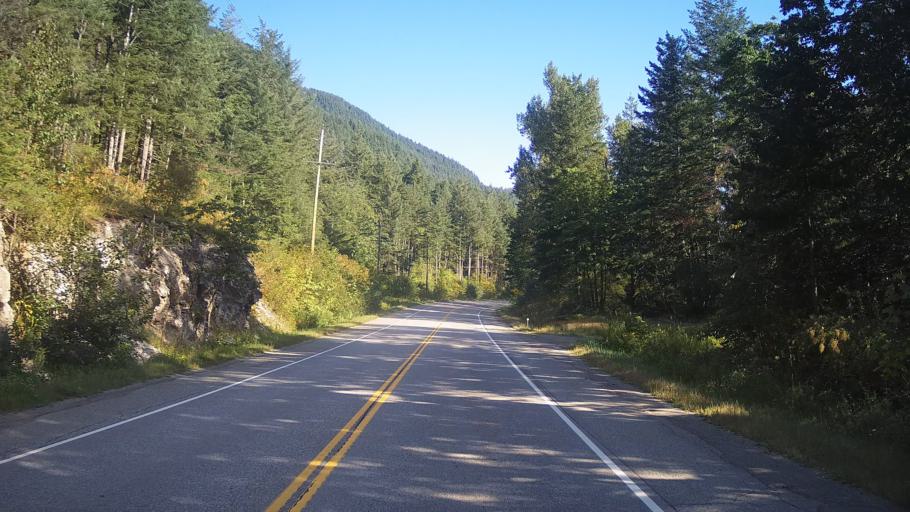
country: CA
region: British Columbia
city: Hope
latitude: 49.4316
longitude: -121.4387
